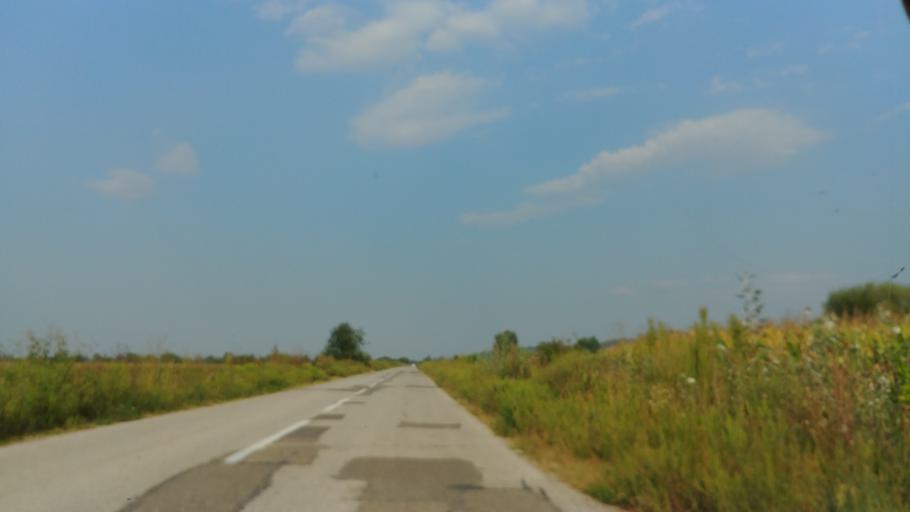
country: BA
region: Republika Srpska
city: Lopare
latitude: 44.7374
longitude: 18.8574
